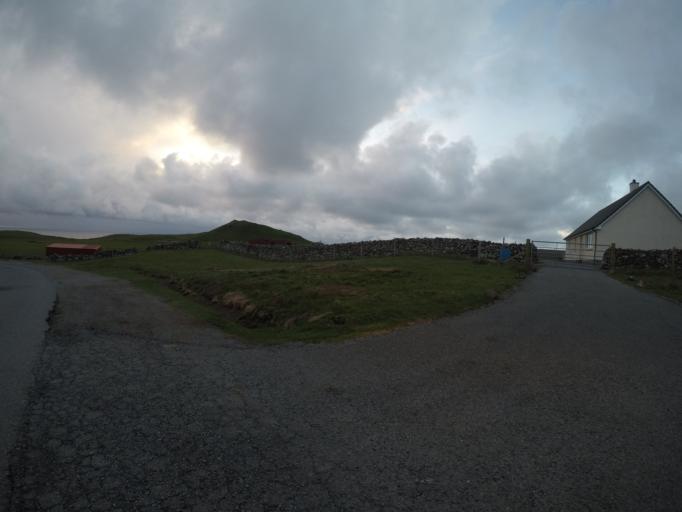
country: GB
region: Scotland
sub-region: Highland
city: Portree
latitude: 57.6821
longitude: -6.3440
